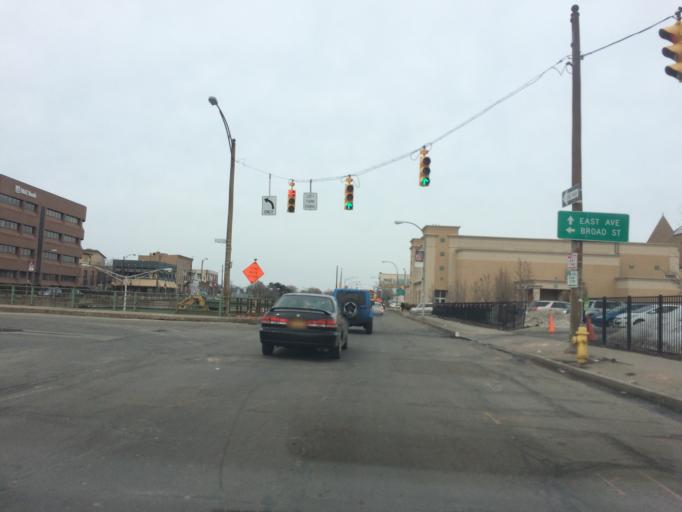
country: US
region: New York
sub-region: Monroe County
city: Rochester
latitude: 43.1543
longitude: -77.5974
